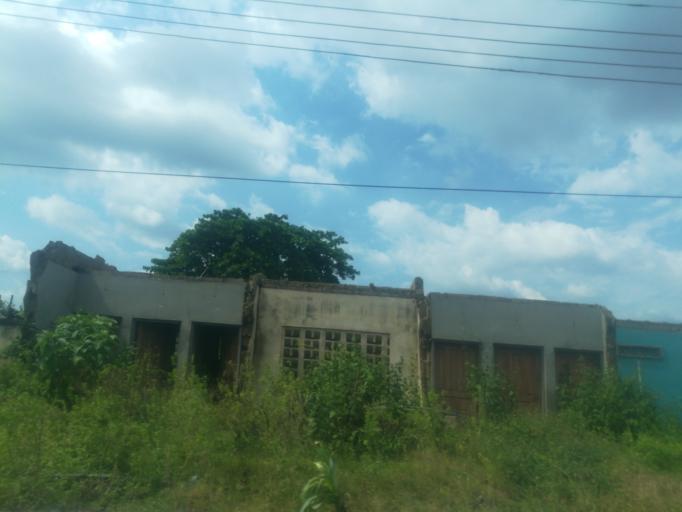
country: NG
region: Oyo
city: Ibadan
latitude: 7.4181
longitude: 3.8576
